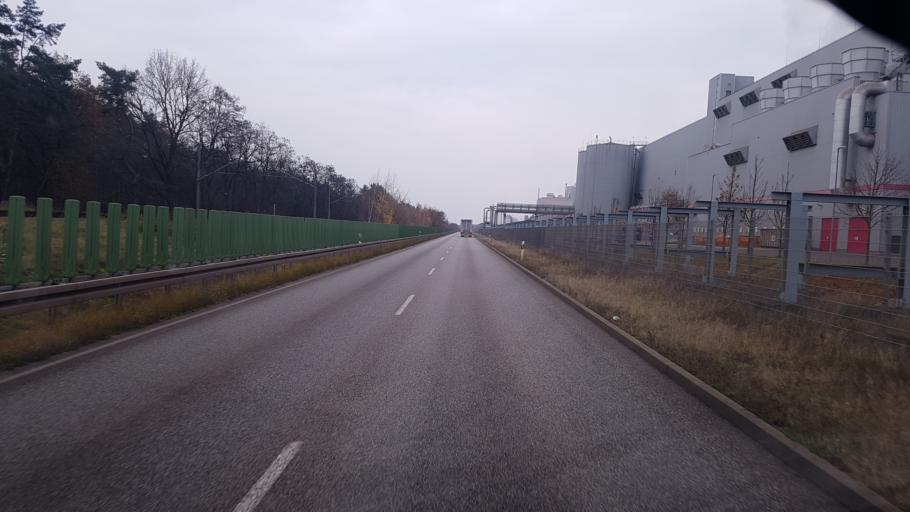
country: DE
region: Brandenburg
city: Ziltendorf
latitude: 52.1801
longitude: 14.6353
